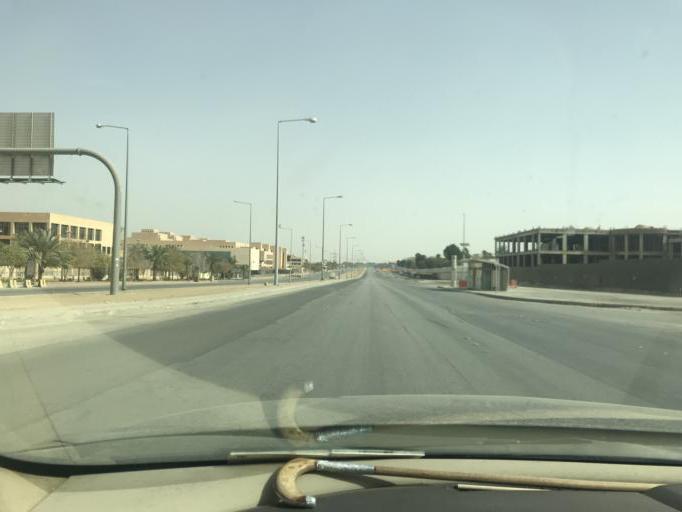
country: SA
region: Ar Riyad
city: Riyadh
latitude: 24.8141
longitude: 46.6896
